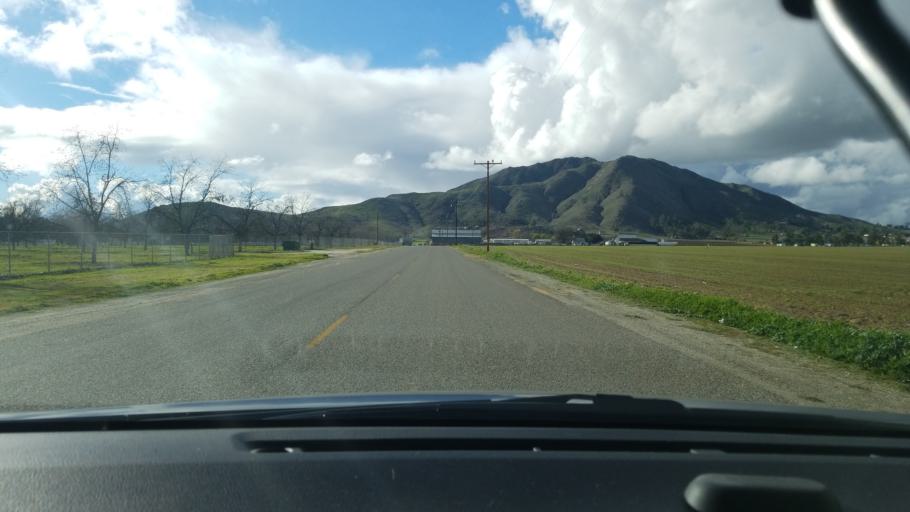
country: US
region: California
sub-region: Riverside County
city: Green Acres
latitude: 33.7220
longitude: -117.0678
